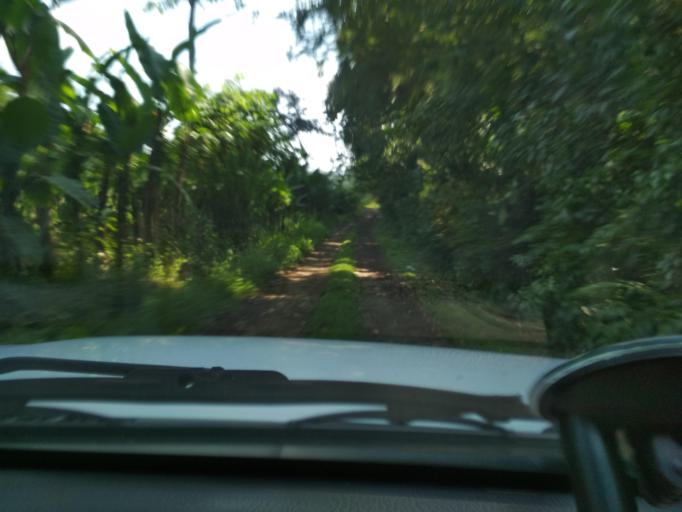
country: MX
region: Veracruz
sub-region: Chocaman
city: San Jose Neria
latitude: 18.9816
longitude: -97.0093
